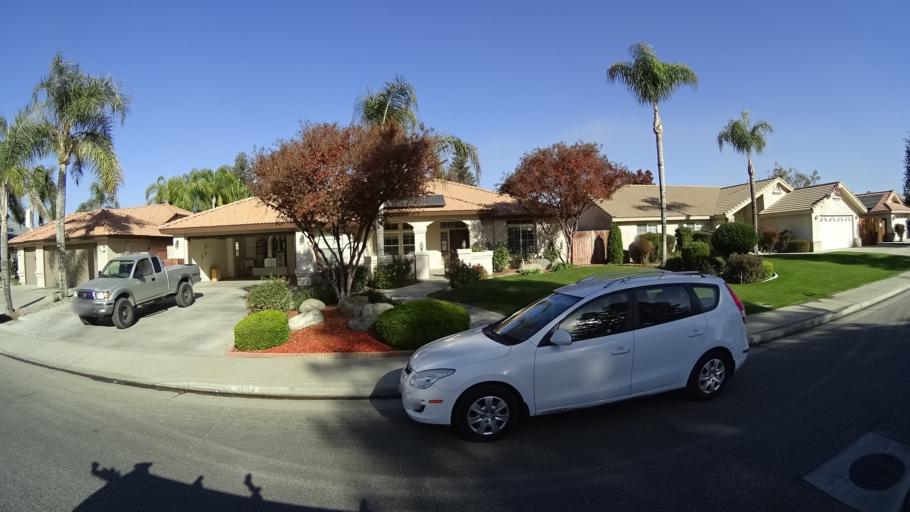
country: US
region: California
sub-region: Kern County
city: Greenfield
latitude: 35.2782
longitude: -119.0417
